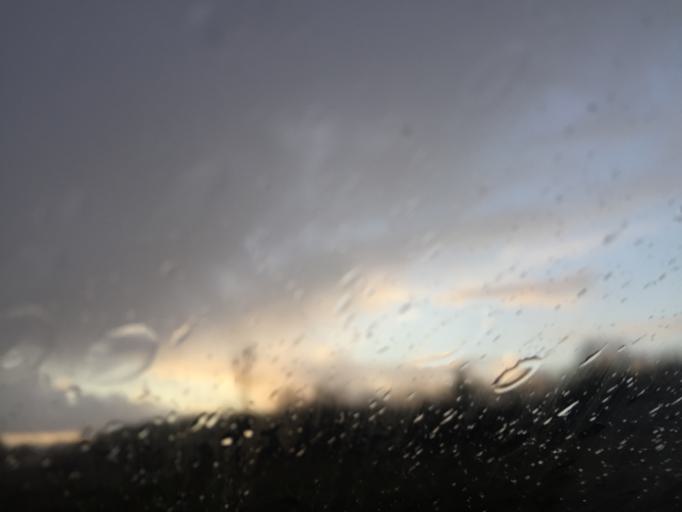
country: LV
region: Burtnieki
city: Matisi
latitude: 57.6812
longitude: 25.2410
